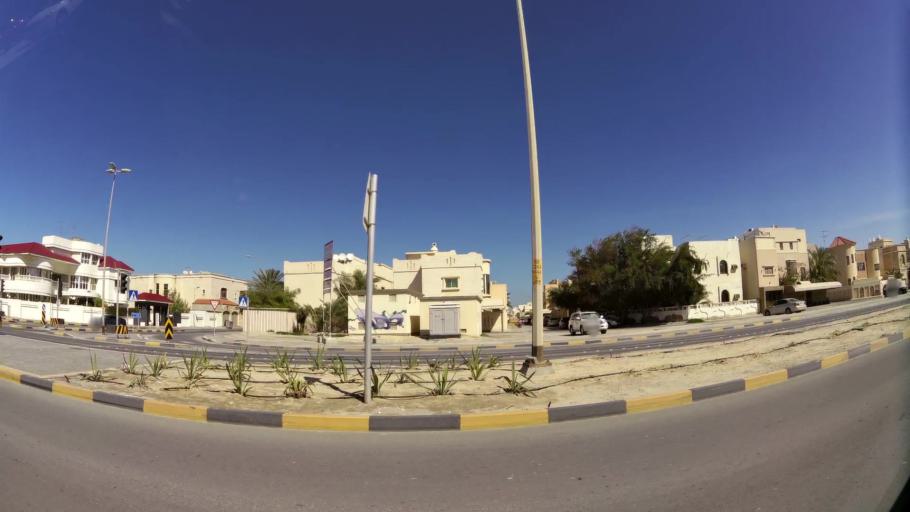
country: BH
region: Muharraq
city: Al Hadd
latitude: 26.2506
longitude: 50.6399
